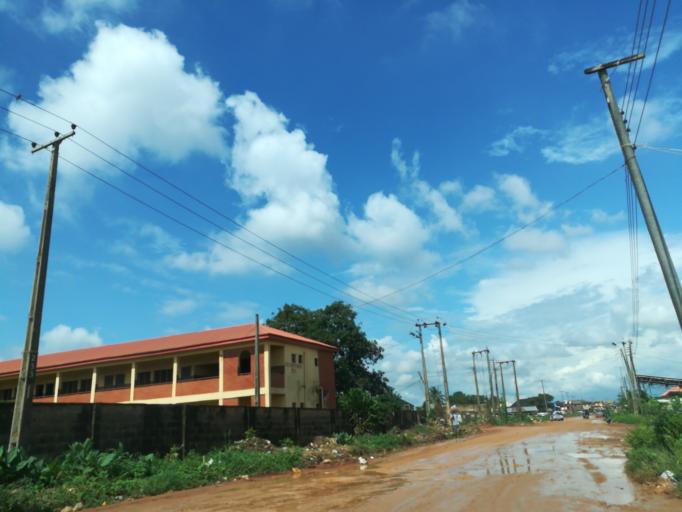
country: NG
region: Lagos
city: Ikorodu
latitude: 6.5926
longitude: 3.5210
